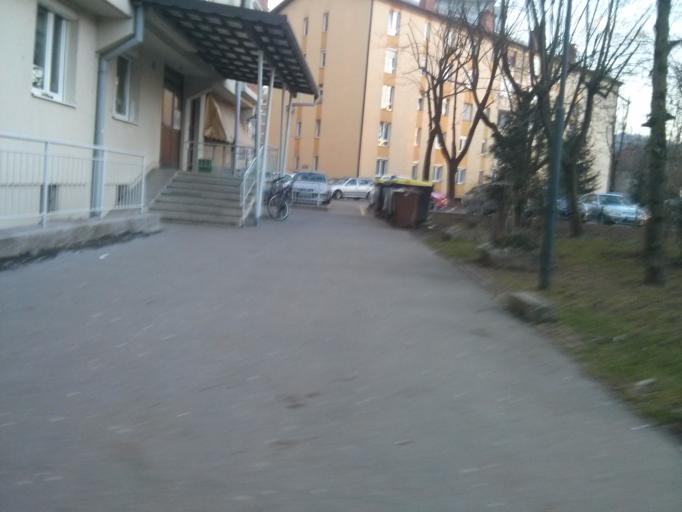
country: SI
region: Ljubljana
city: Ljubljana
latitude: 46.0729
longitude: 14.4850
